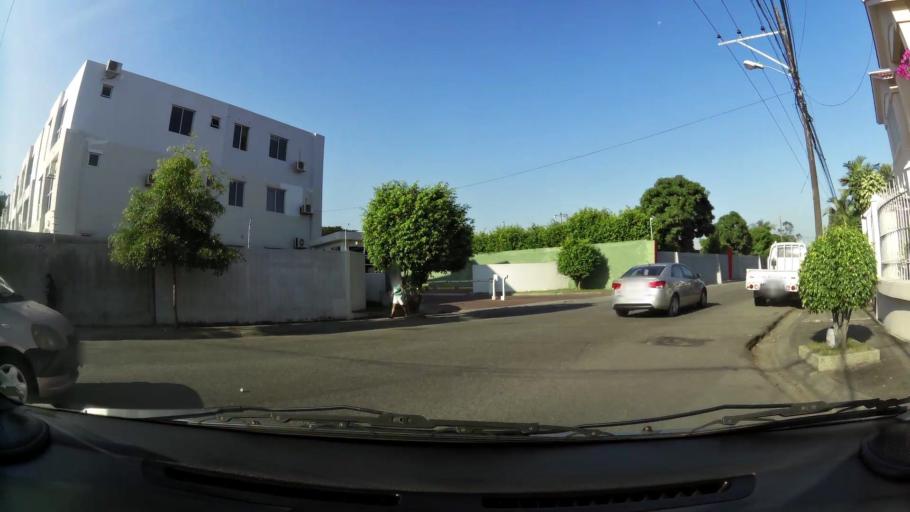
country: EC
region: Guayas
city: Santa Lucia
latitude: -2.1883
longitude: -79.9648
